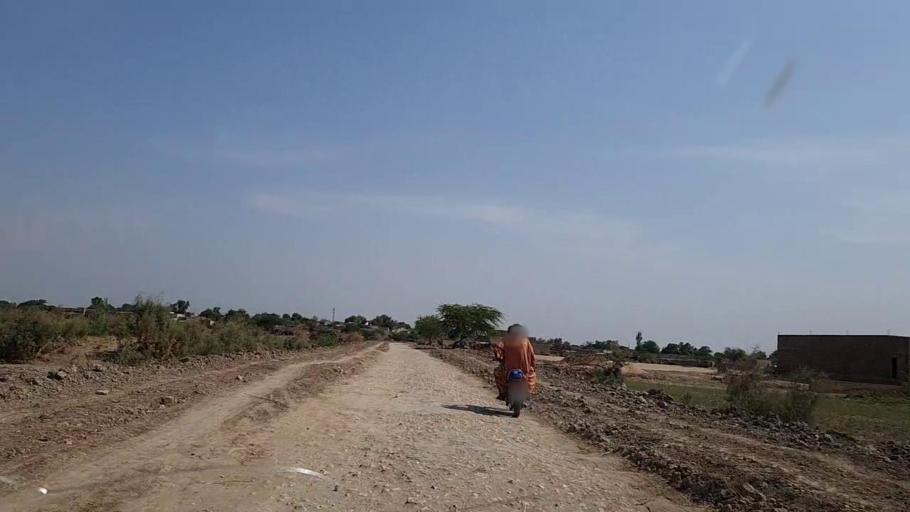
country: PK
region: Sindh
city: Khanpur
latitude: 27.7527
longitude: 69.3372
